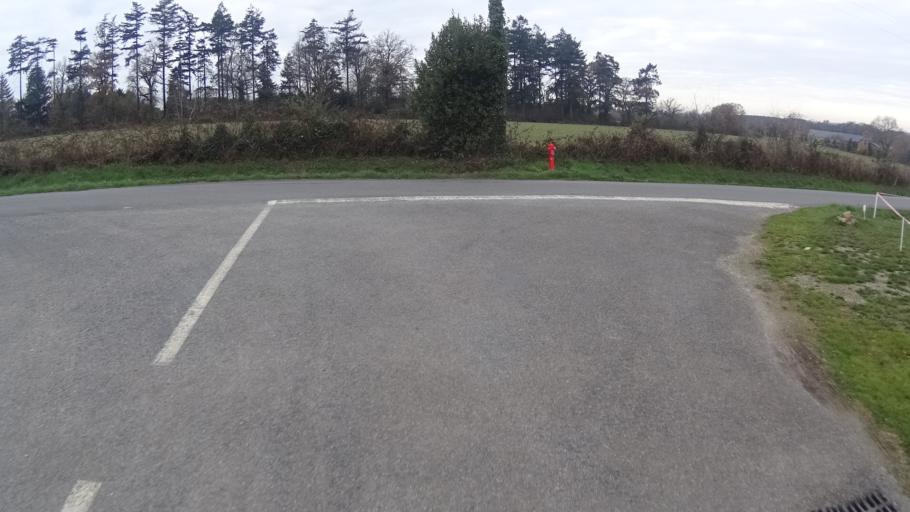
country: FR
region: Pays de la Loire
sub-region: Departement de la Loire-Atlantique
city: Avessac
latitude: 47.6516
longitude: -1.9943
